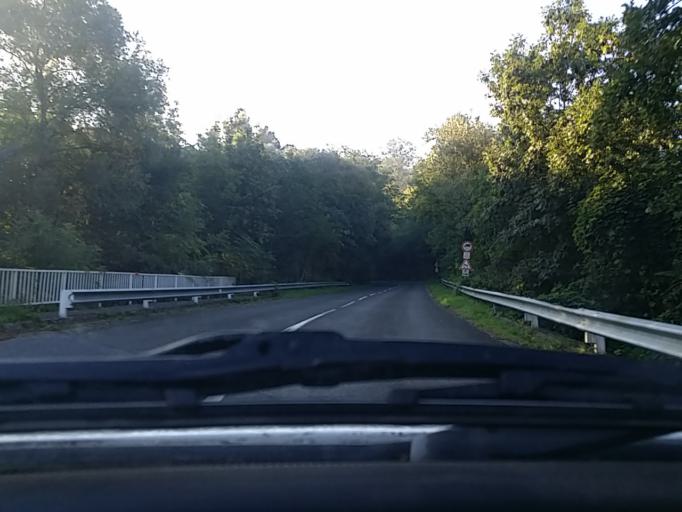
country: HU
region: Pest
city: Visegrad
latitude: 47.7651
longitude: 18.9539
